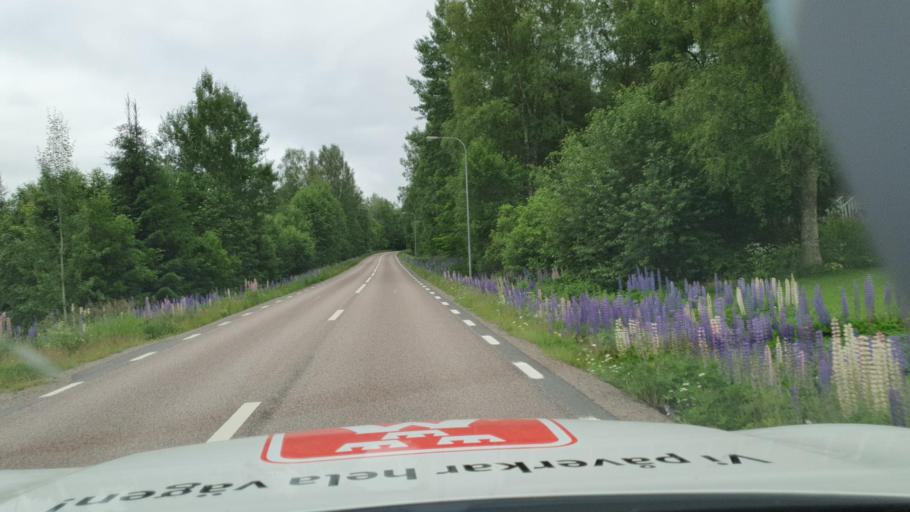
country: SE
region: Vaermland
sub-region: Sunne Kommun
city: Sunne
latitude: 59.8869
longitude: 12.9230
